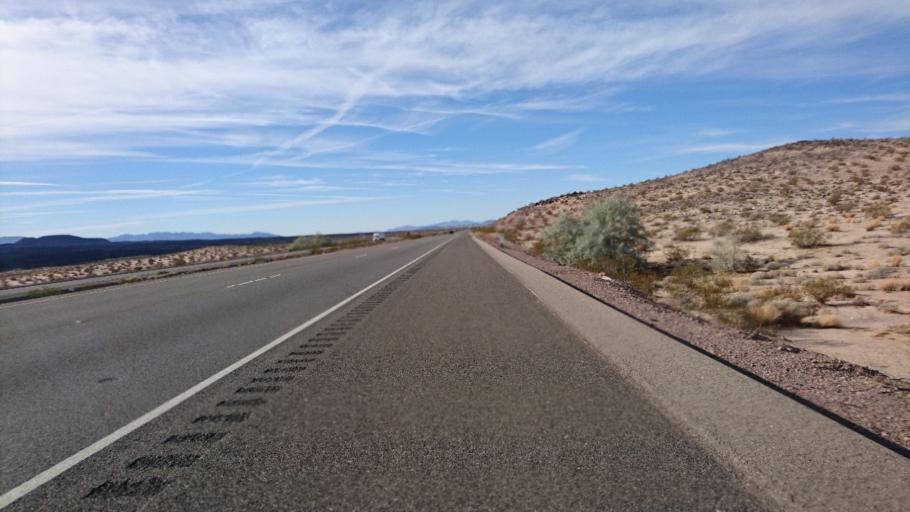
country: US
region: California
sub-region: San Bernardino County
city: Joshua Tree
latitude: 34.7491
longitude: -116.3320
